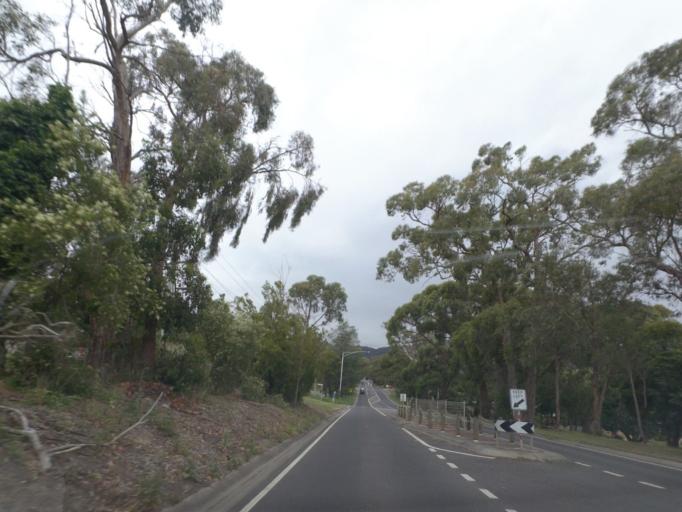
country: AU
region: Victoria
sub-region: Yarra Ranges
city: Kilsyth
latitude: -37.8092
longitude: 145.3303
